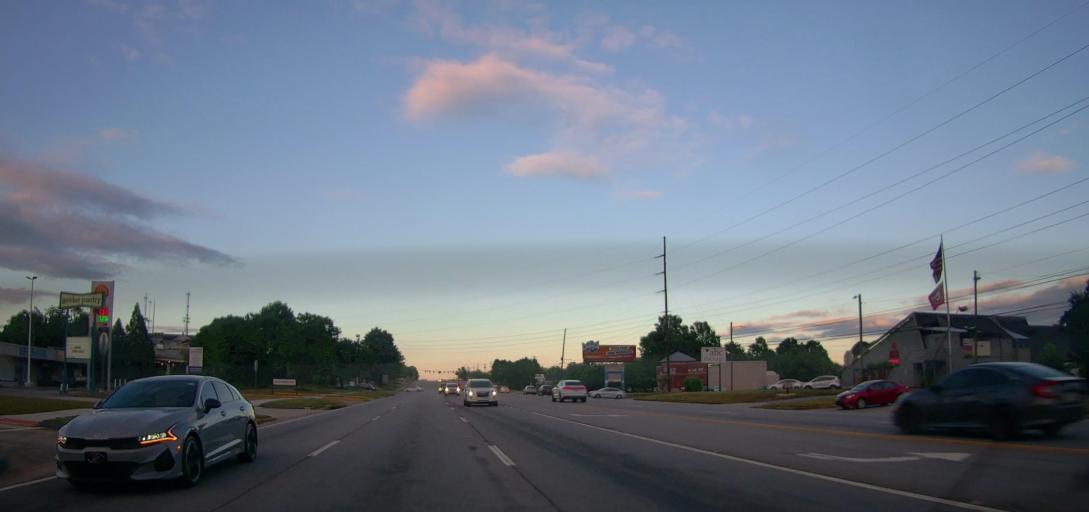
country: US
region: Georgia
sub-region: Clarke County
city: Athens
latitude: 33.9486
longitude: -83.4147
